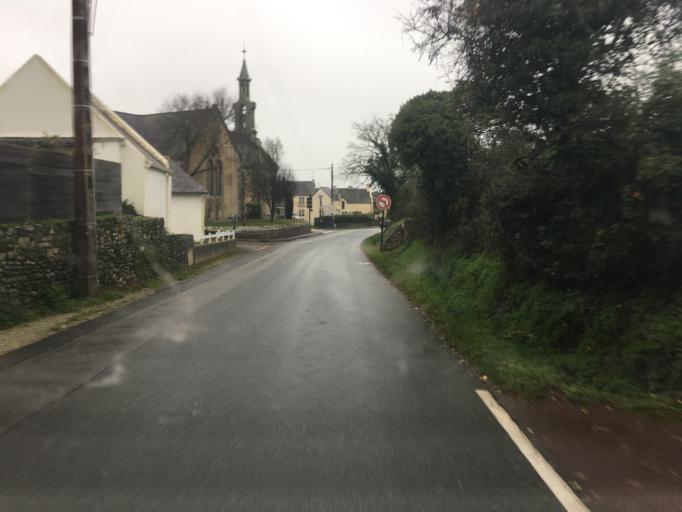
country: FR
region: Brittany
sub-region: Departement du Morbihan
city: Sarzeau
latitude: 47.5076
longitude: -2.6852
